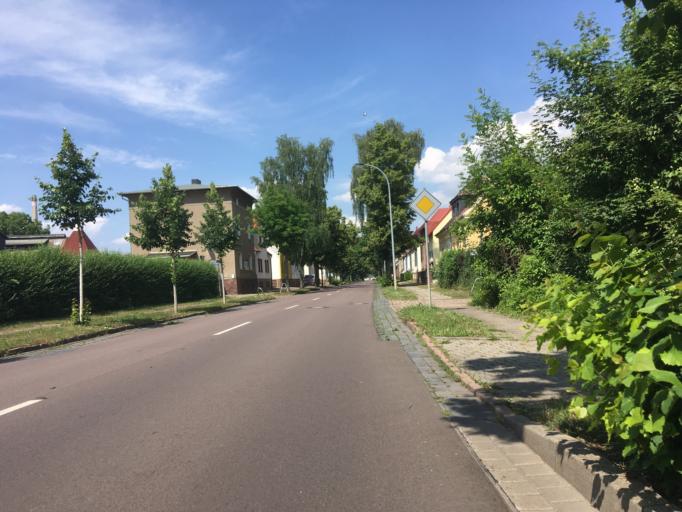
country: DE
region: Saxony-Anhalt
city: Koethen
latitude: 51.7527
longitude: 12.0095
